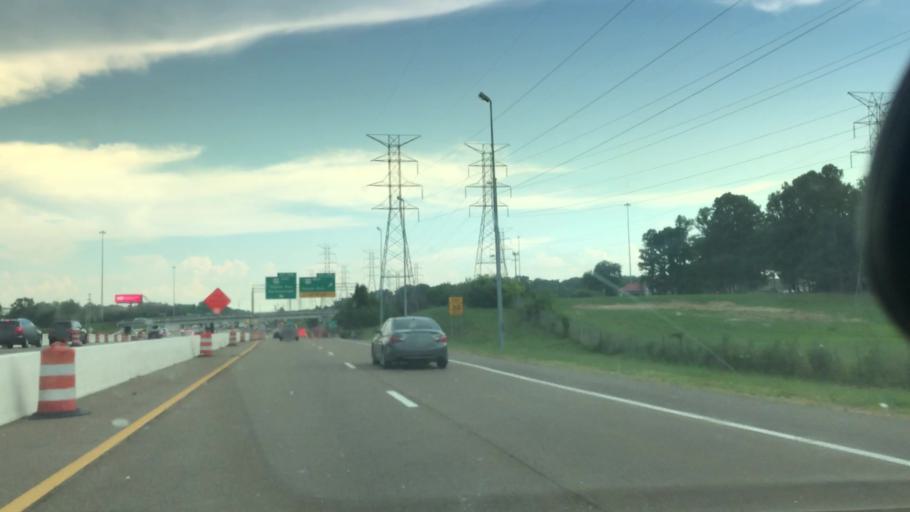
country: US
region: Tennessee
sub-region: Shelby County
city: Germantown
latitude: 35.1070
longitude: -89.8703
